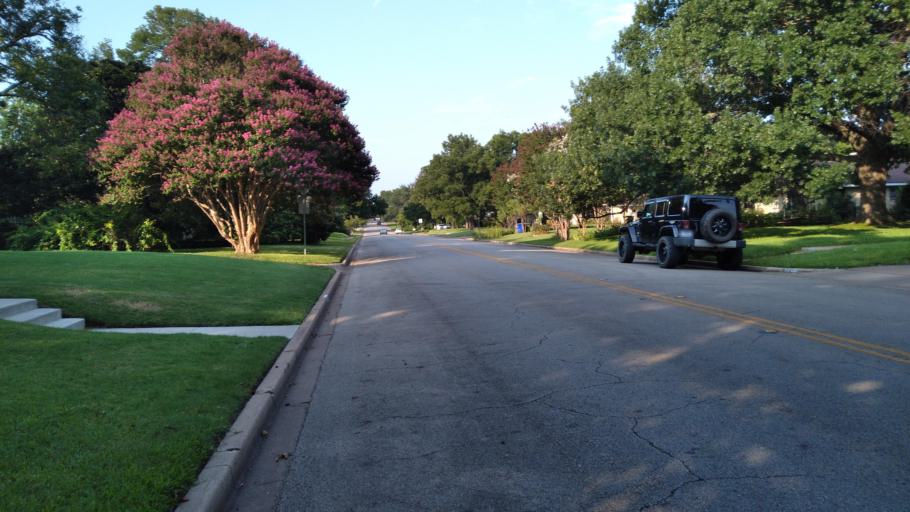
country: US
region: Texas
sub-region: McLennan County
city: Beverly Hills
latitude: 31.5306
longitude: -97.1617
